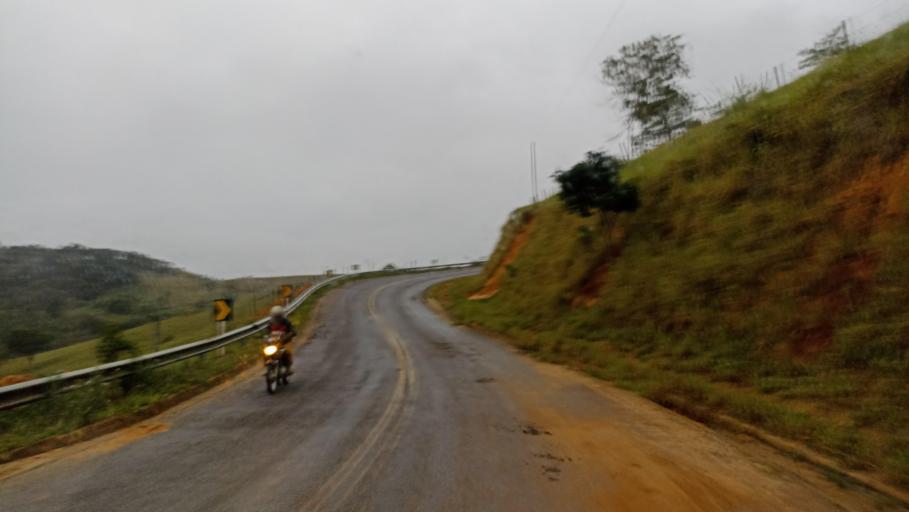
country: BR
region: Bahia
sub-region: Itanhem
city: Itanhem
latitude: -16.7323
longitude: -40.4377
